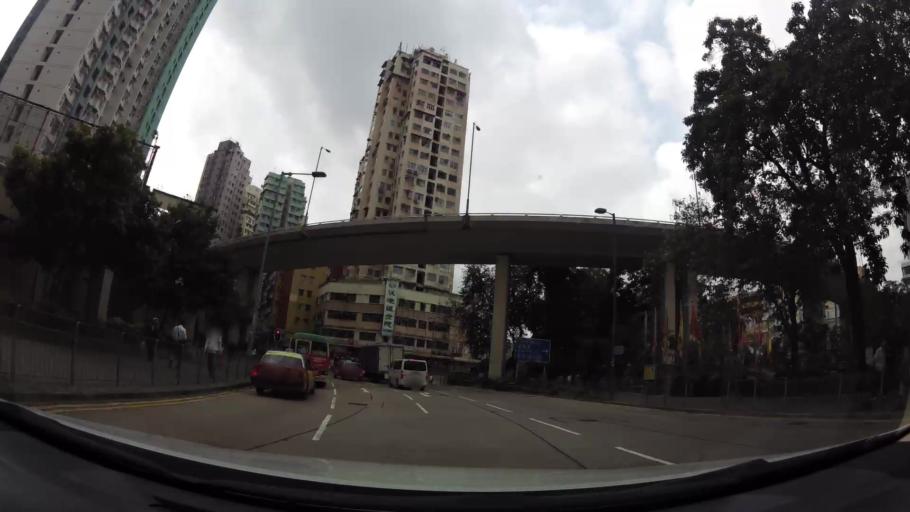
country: HK
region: Kowloon City
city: Kowloon
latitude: 22.3198
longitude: 114.2153
